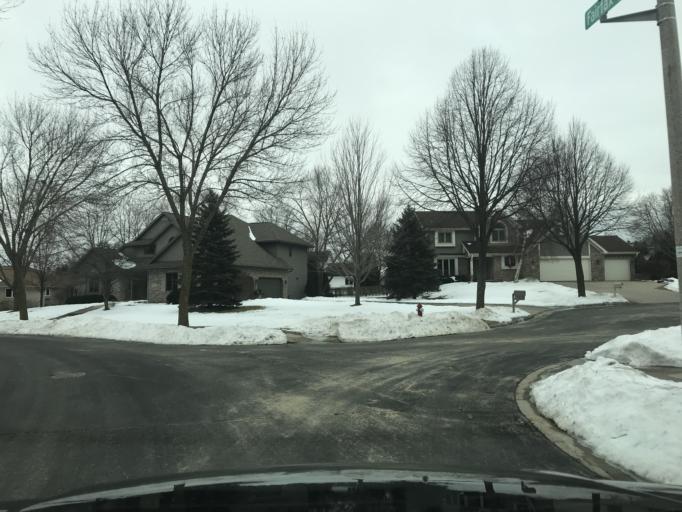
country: US
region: Wisconsin
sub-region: Dane County
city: Monona
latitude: 43.0826
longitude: -89.2746
